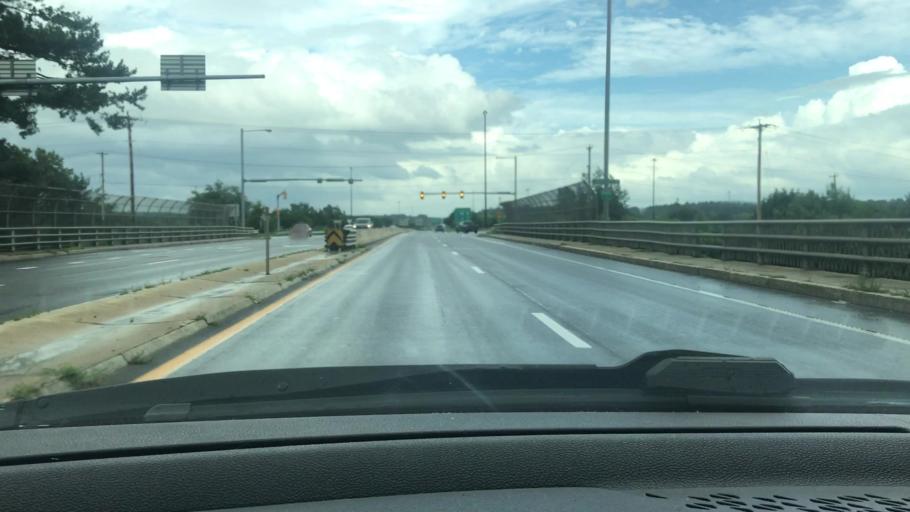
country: US
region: New Hampshire
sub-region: Merrimack County
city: Concord
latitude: 43.2147
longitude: -71.5397
